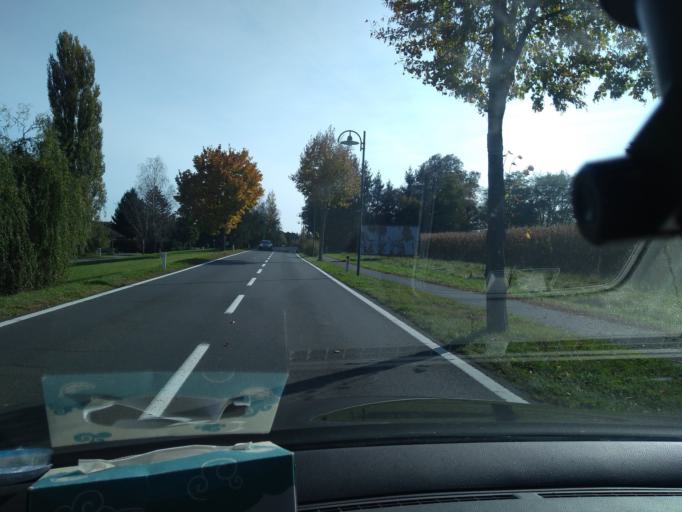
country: AT
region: Styria
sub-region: Politischer Bezirk Leibnitz
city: Kaindorf an der Sulm
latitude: 46.8238
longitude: 15.5448
